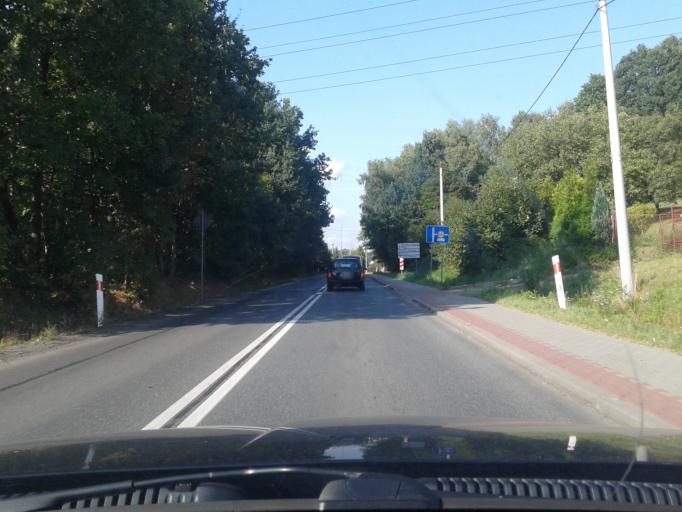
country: PL
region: Silesian Voivodeship
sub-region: Powiat wodzislawski
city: Wodzislaw Slaski
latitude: 49.9904
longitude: 18.4551
